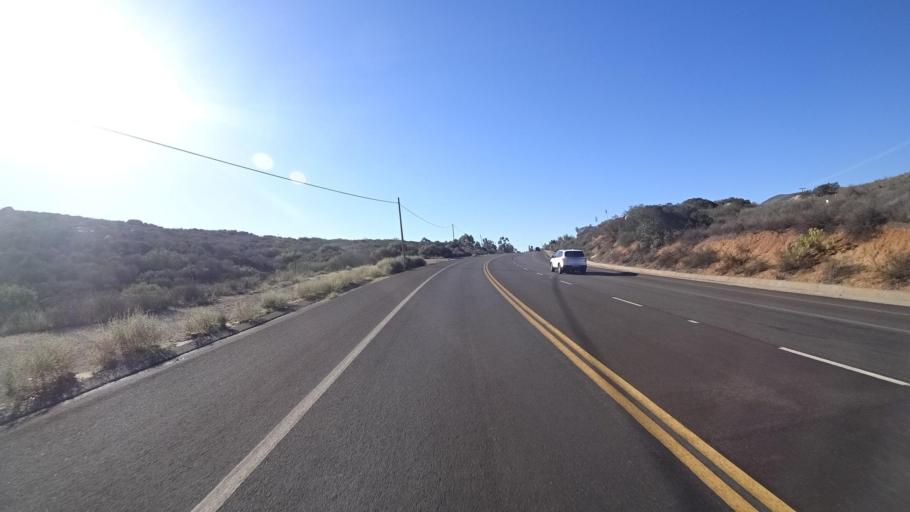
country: MX
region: Baja California
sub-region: Tijuana
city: Villa del Campo
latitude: 32.6261
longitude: -116.7647
